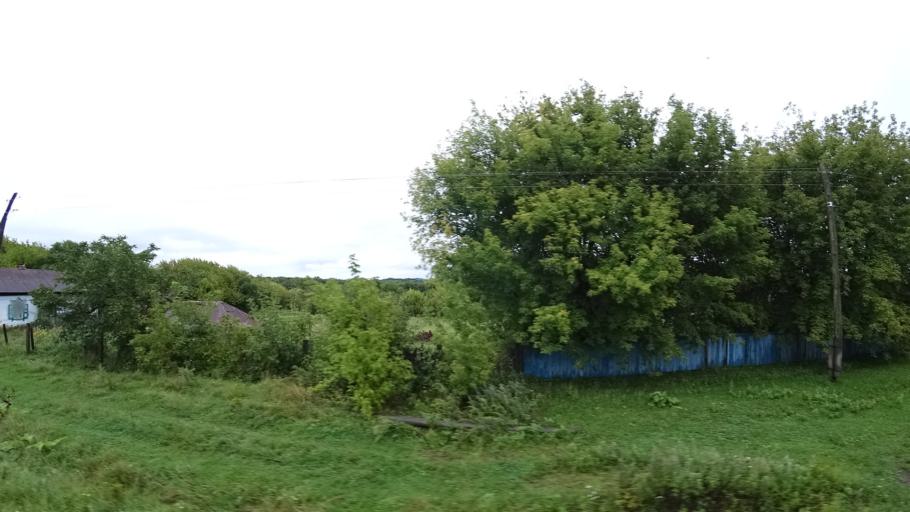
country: RU
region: Primorskiy
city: Monastyrishche
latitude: 44.2671
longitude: 132.4202
